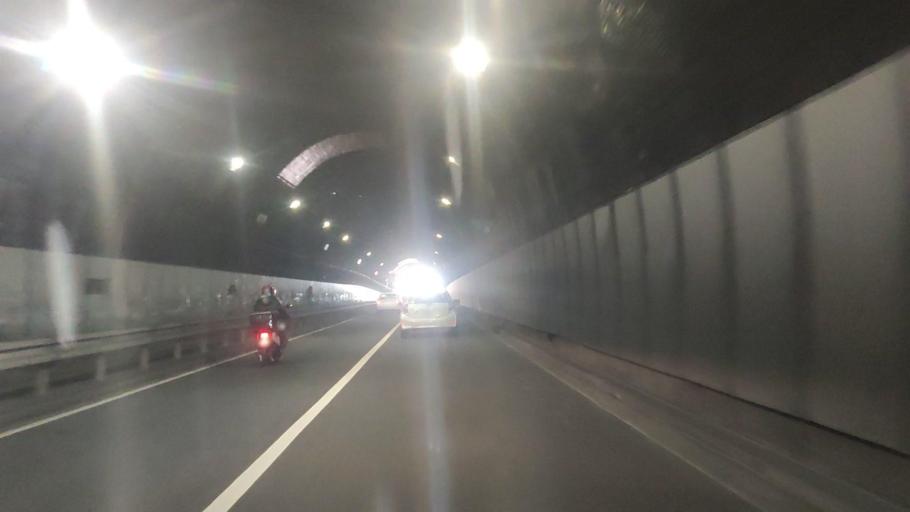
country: JP
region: Oita
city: Oita
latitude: 33.2209
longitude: 131.5949
